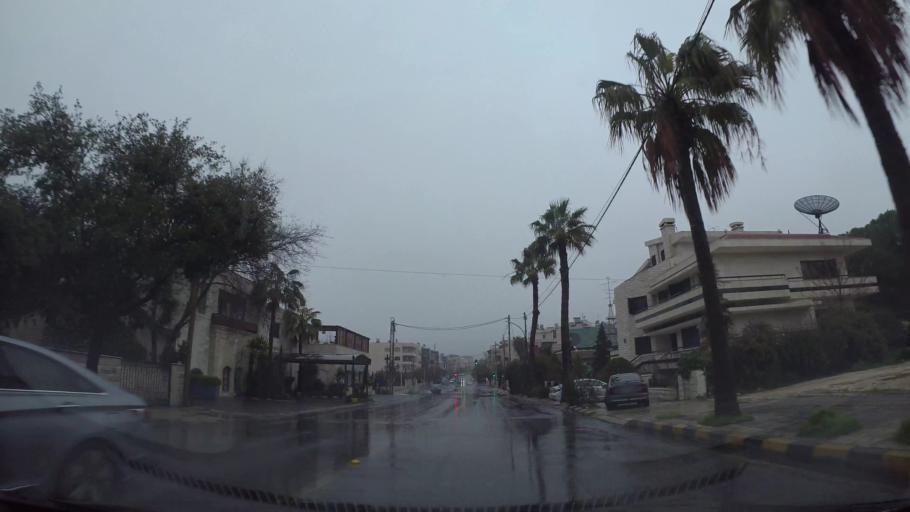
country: JO
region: Amman
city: Wadi as Sir
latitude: 31.9673
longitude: 35.8709
